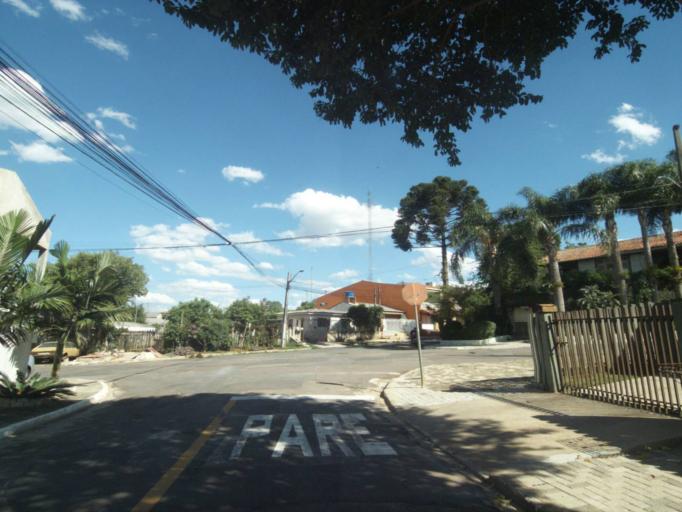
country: BR
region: Parana
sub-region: Curitiba
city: Curitiba
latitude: -25.4999
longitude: -49.3187
